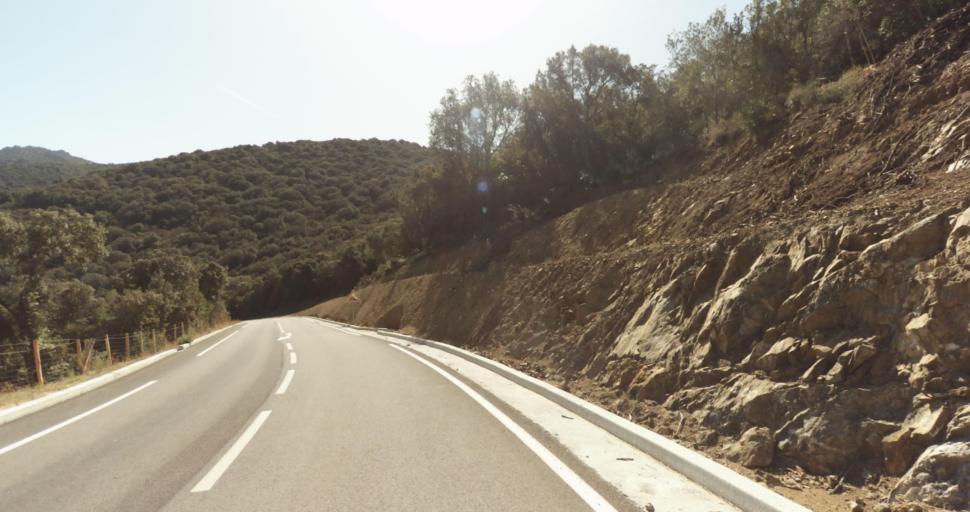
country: FR
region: Corsica
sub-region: Departement de la Corse-du-Sud
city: Ajaccio
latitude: 41.9245
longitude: 8.6457
